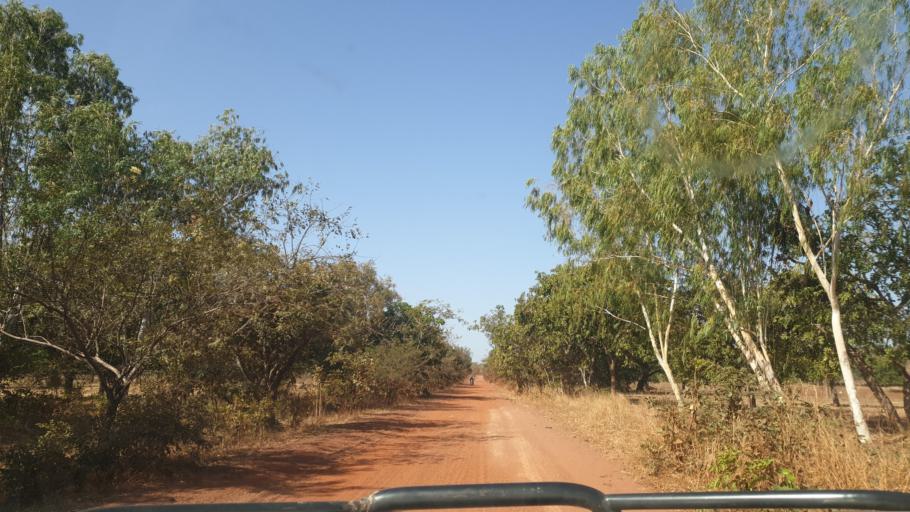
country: ML
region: Sikasso
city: Bougouni
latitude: 11.8207
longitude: -6.9547
